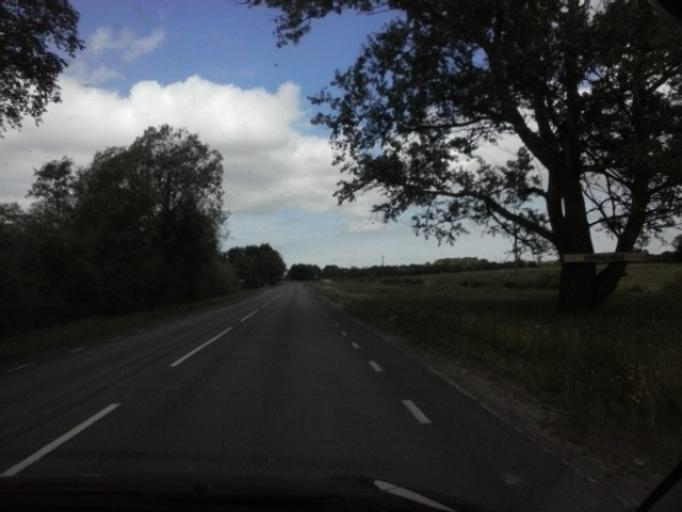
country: EE
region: Laeaene
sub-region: Ridala Parish
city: Uuemoisa
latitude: 58.9583
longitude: 23.7829
